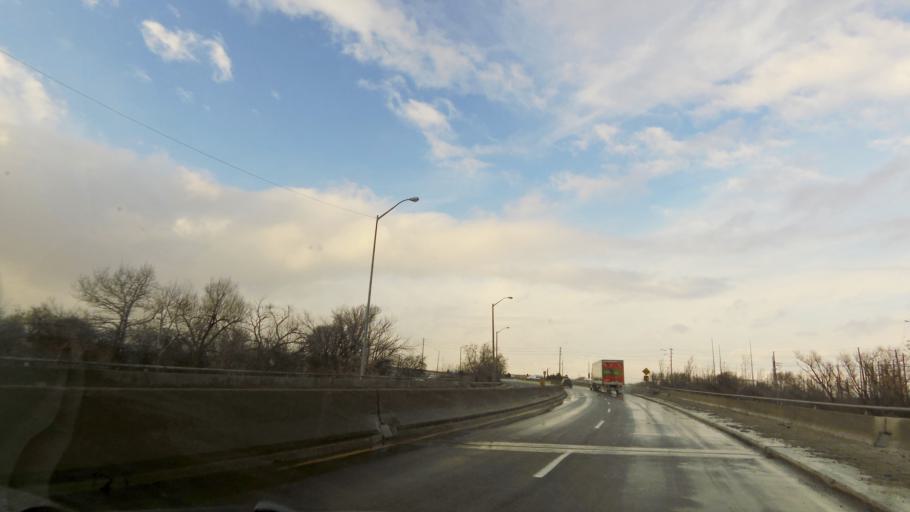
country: CA
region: Ontario
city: Brampton
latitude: 43.6767
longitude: -79.6904
